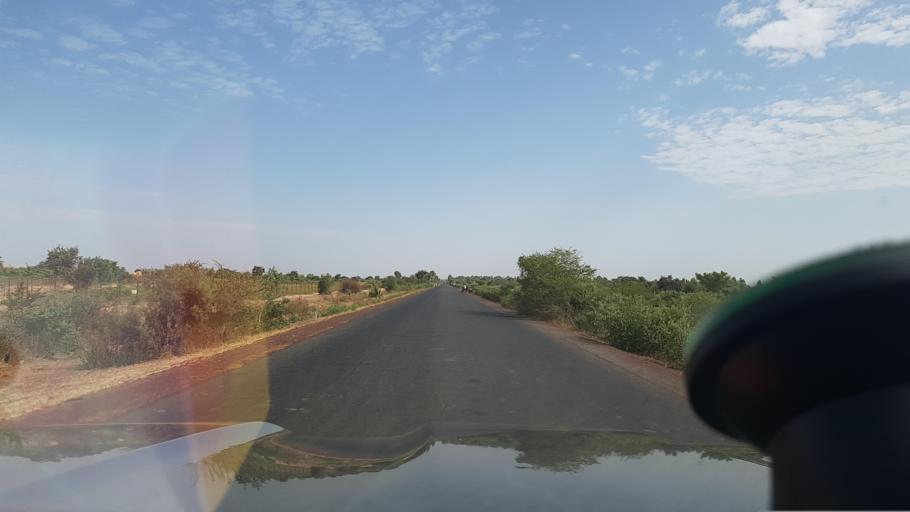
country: ML
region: Segou
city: Markala
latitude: 13.7010
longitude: -6.0949
